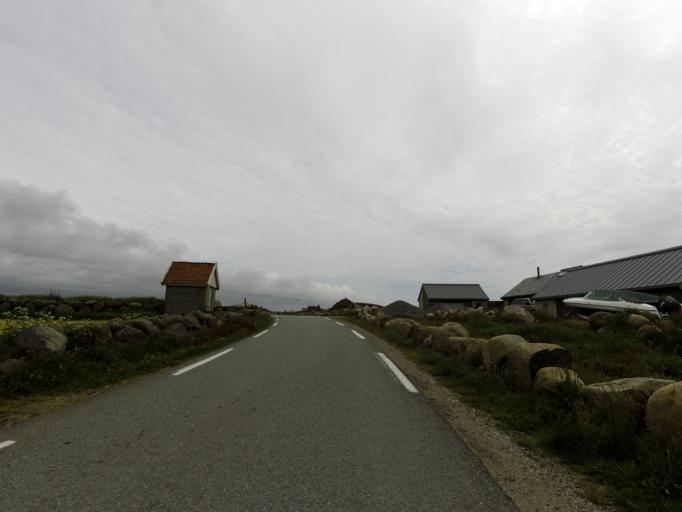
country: NO
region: Rogaland
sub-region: Ha
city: Naerbo
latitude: 58.6655
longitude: 5.5527
